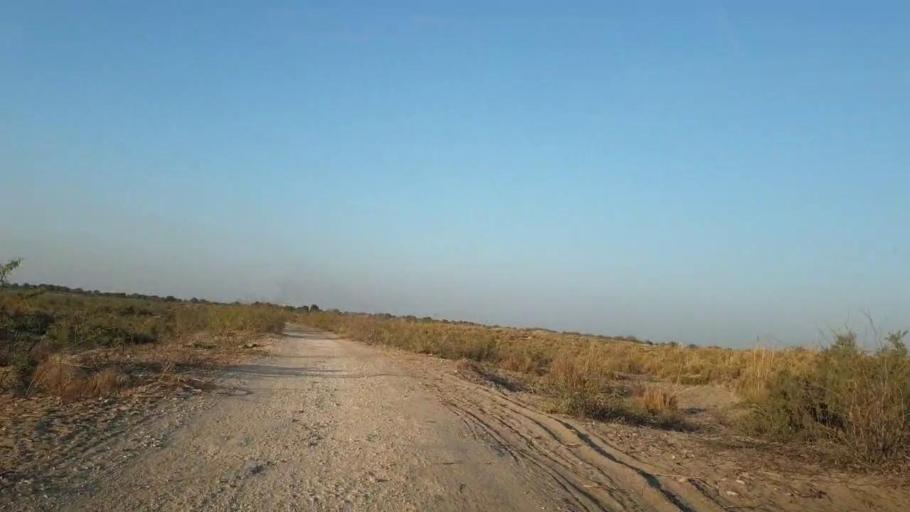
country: PK
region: Sindh
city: Mirpur Khas
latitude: 25.6826
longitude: 69.0500
